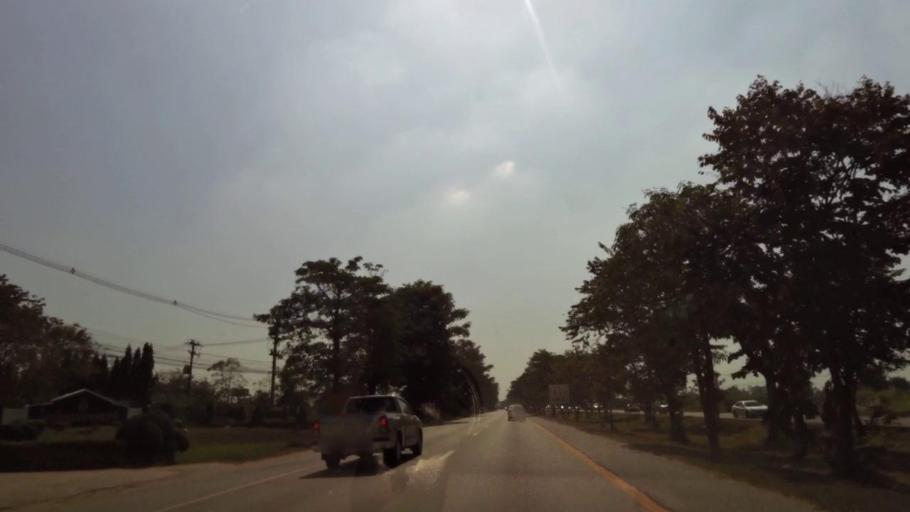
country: TH
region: Phichit
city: Wachira Barami
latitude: 16.5177
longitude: 100.1429
